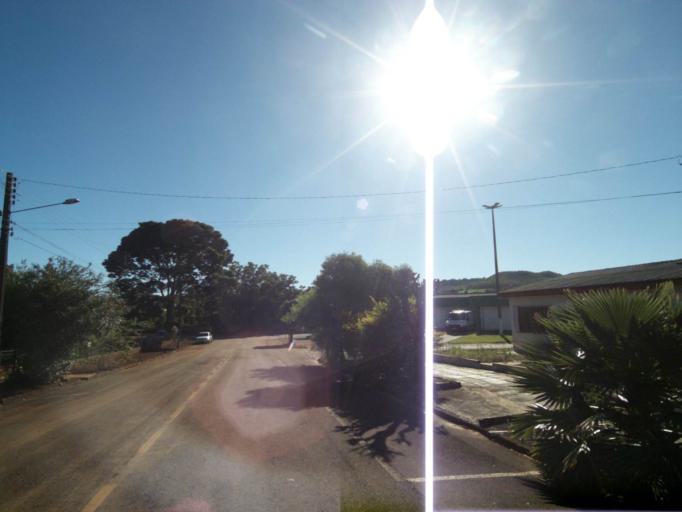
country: BR
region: Santa Catarina
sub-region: Sao Lourenco Do Oeste
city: Sao Lourenco dOeste
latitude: -26.2646
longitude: -52.7839
